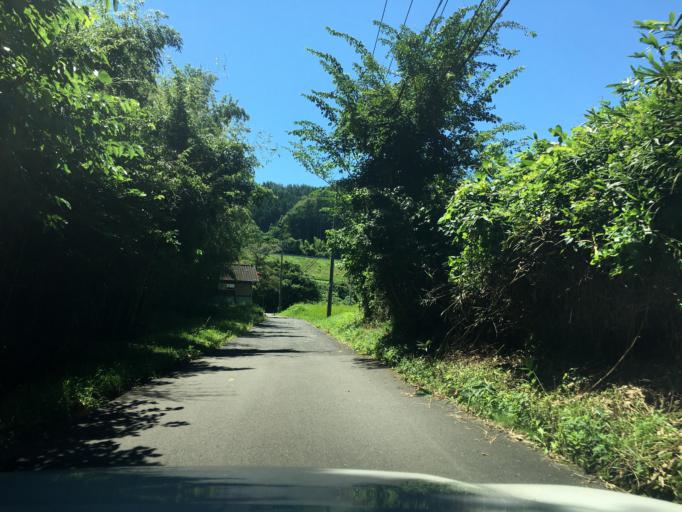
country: JP
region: Fukushima
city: Ishikawa
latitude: 37.2083
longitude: 140.5231
